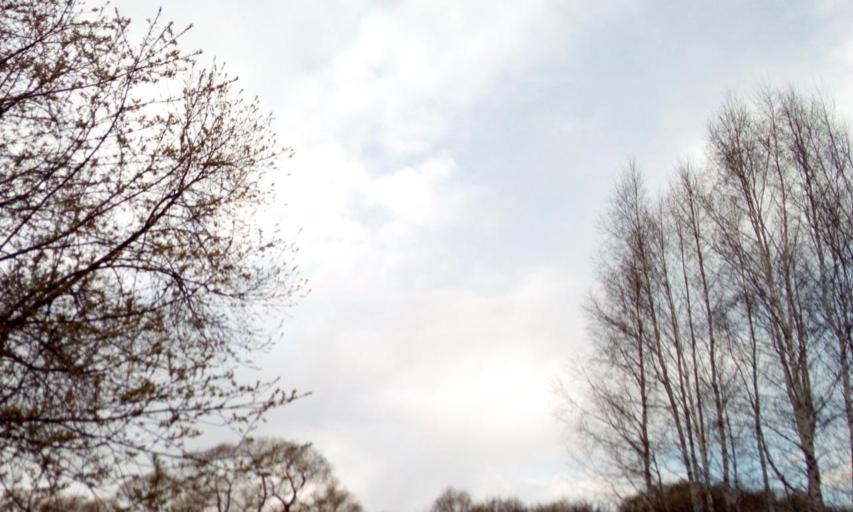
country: RU
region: Moskovskaya
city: Troitsk
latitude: 55.5159
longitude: 37.2636
